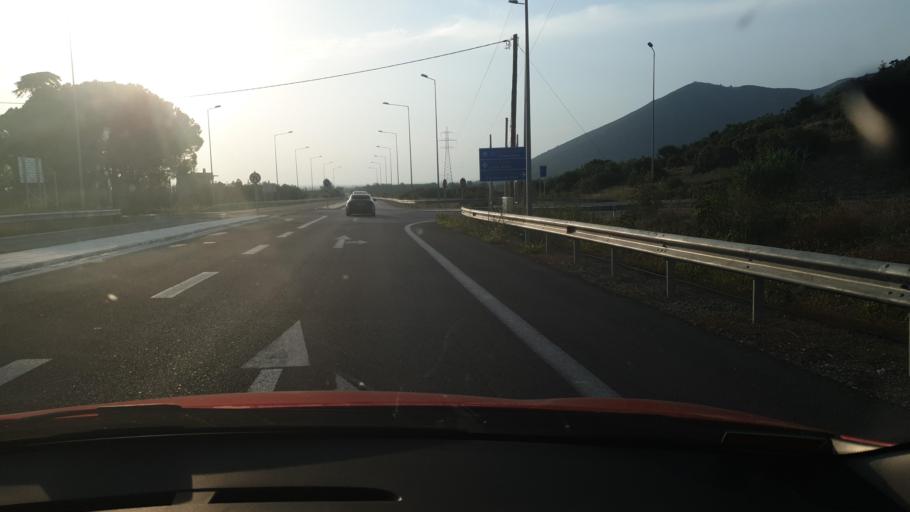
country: GR
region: Central Macedonia
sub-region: Nomos Thessalonikis
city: Vasilika
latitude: 40.4666
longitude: 23.1980
